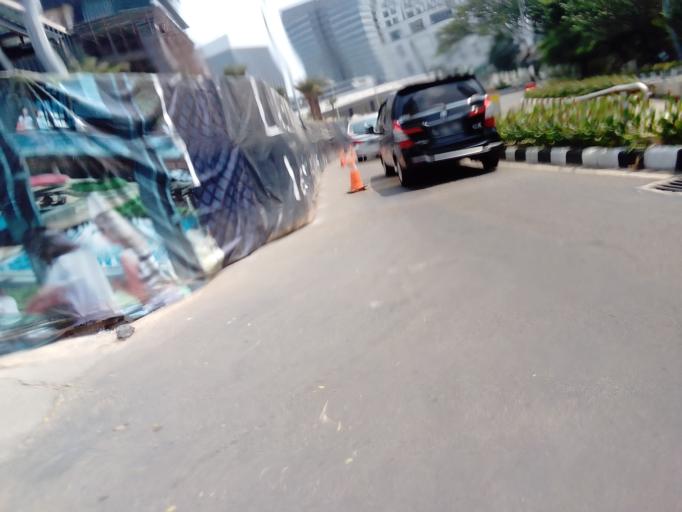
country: ID
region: Jakarta Raya
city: Jakarta
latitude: -6.2271
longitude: 106.8076
